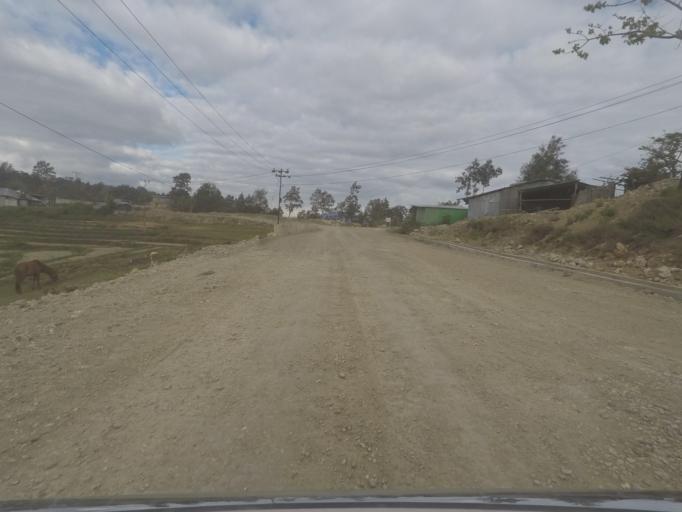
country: TL
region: Baucau
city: Venilale
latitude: -8.6345
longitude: 126.3781
